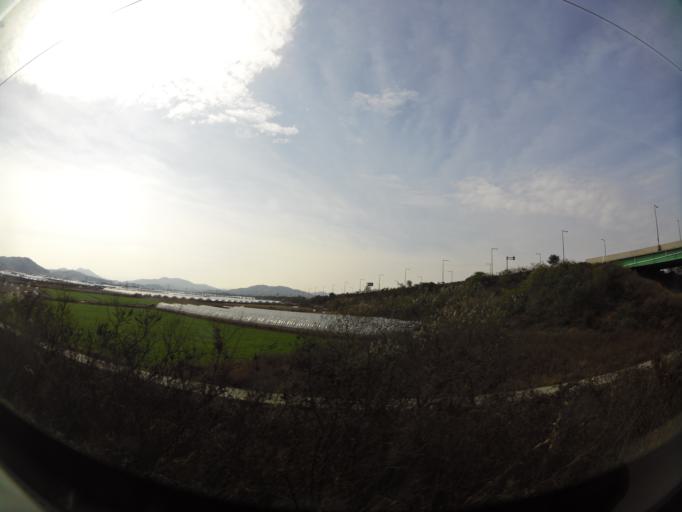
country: KR
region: Daejeon
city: Songgang-dong
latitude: 36.5699
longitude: 127.3159
